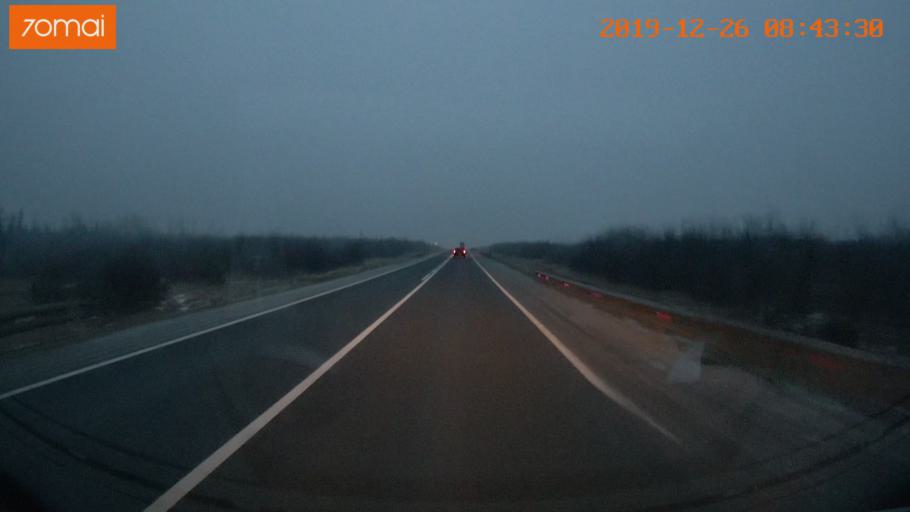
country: RU
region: Jaroslavl
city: Prechistoye
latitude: 58.5736
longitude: 40.3530
